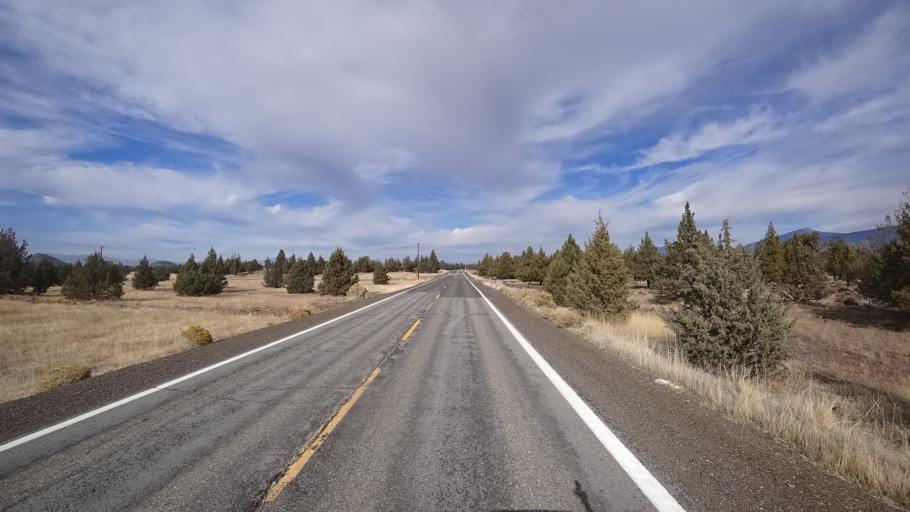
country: US
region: California
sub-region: Siskiyou County
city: Weed
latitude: 41.5870
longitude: -122.4000
